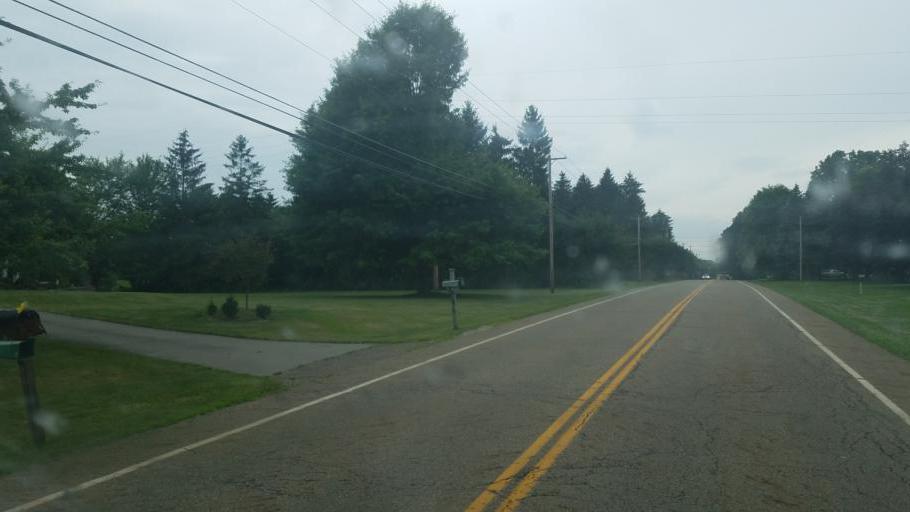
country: US
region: Ohio
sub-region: Summit County
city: Manchester
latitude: 40.9315
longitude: -81.5998
